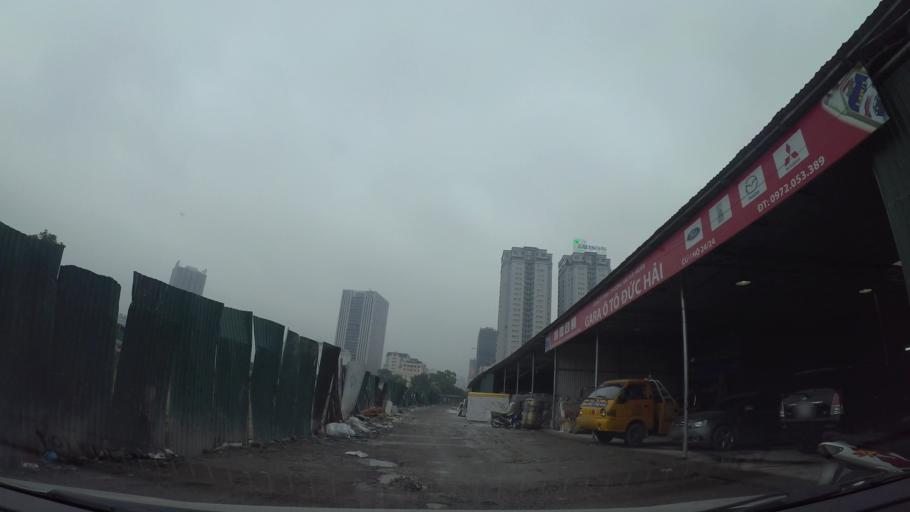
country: VN
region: Ha Noi
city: Cau Giay
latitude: 21.0214
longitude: 105.7845
